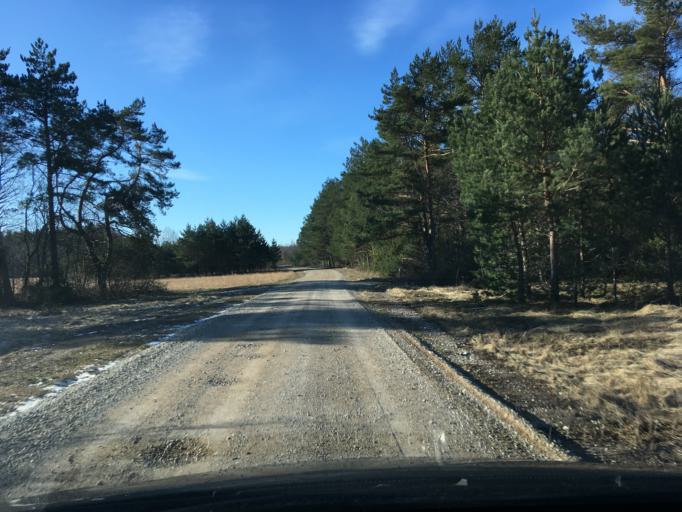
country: EE
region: Laeaene
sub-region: Lihula vald
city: Lihula
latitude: 58.5752
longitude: 23.6989
